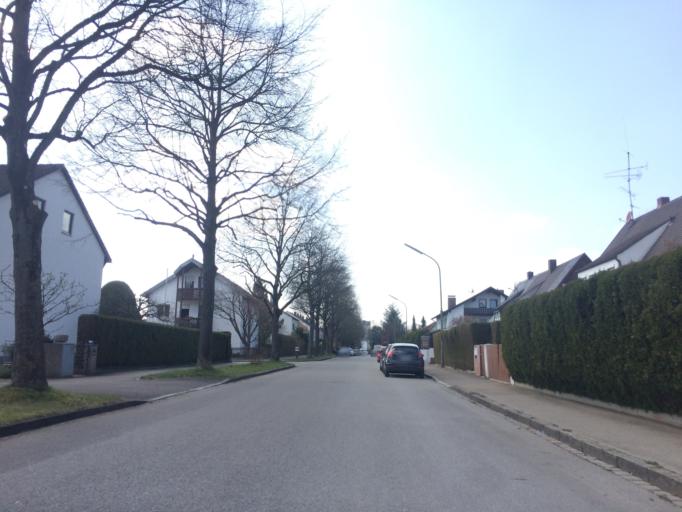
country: DE
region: Bavaria
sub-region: Swabia
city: Augsburg
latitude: 48.3986
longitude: 10.9011
